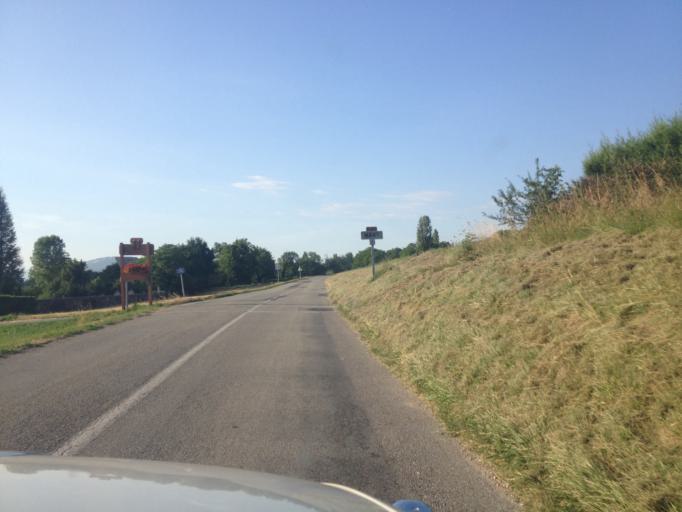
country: FR
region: Rhone-Alpes
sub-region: Departement de la Savoie
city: Mery
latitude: 45.6447
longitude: 5.9340
